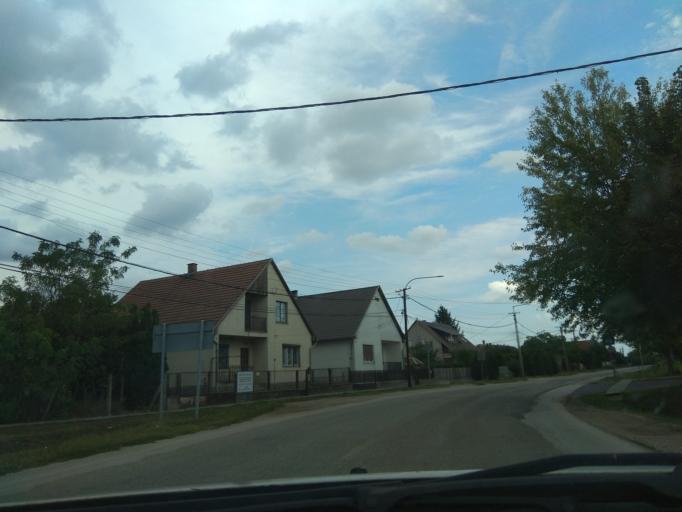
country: HU
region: Borsod-Abauj-Zemplen
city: Malyi
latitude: 48.0408
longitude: 20.8394
